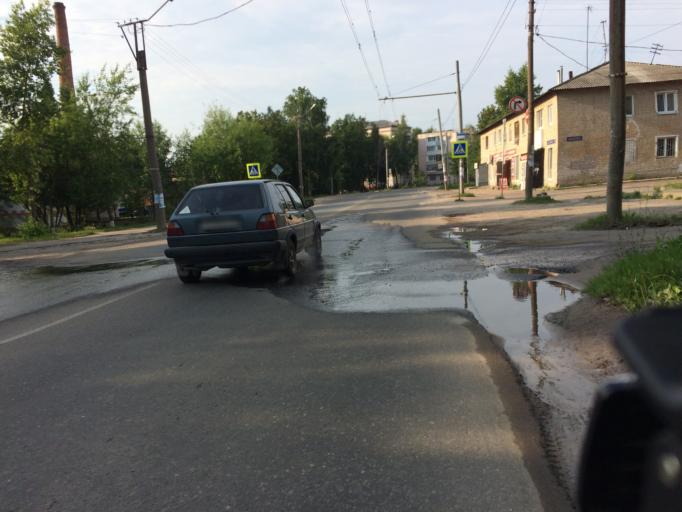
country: RU
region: Mariy-El
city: Yoshkar-Ola
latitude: 56.6285
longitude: 47.9472
